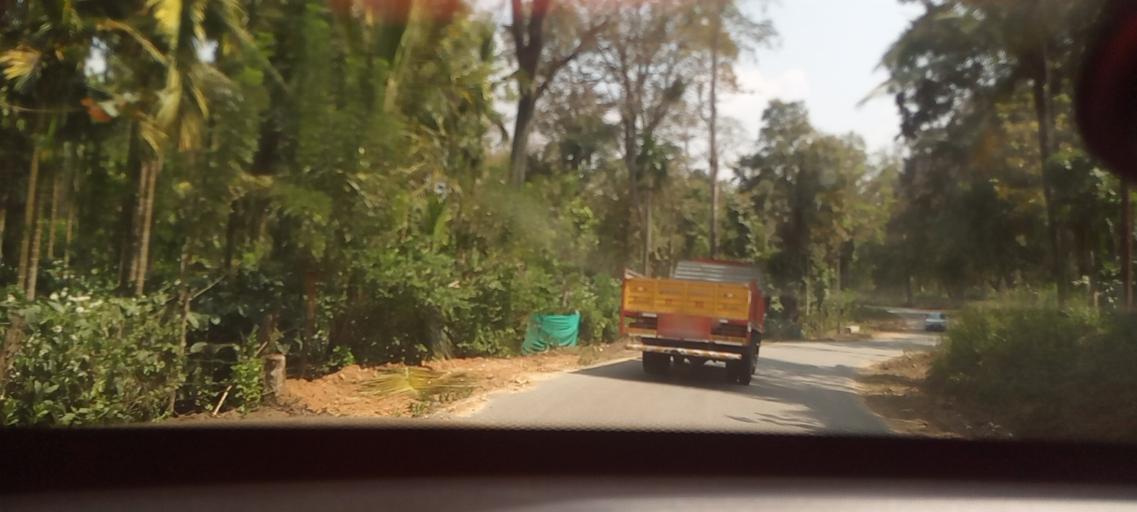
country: IN
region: Karnataka
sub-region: Chikmagalur
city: Mudigere
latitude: 13.3229
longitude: 75.5644
